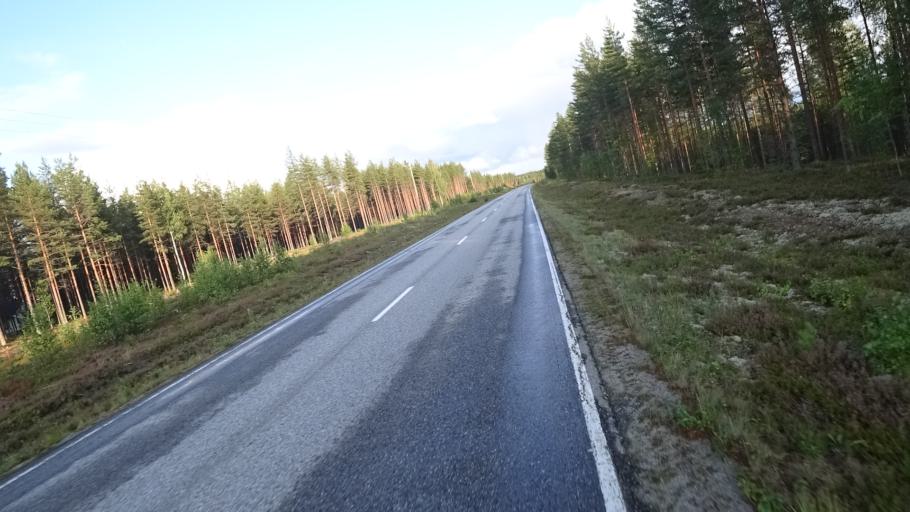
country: FI
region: North Karelia
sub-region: Joensuu
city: Ilomantsi
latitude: 62.6392
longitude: 31.0803
